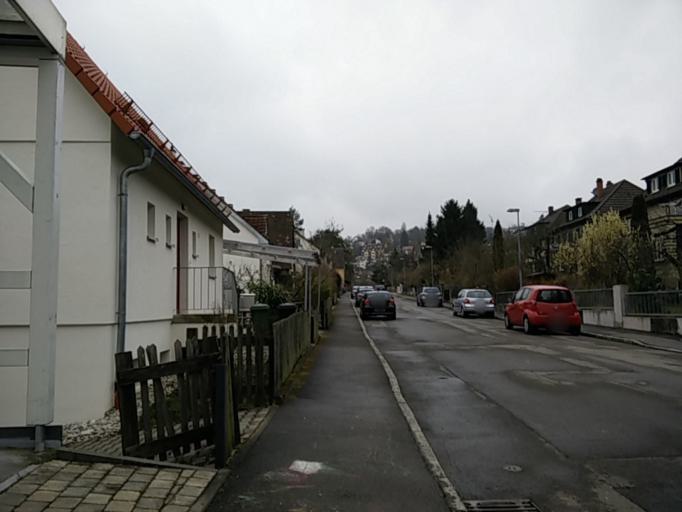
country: DE
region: Baden-Wuerttemberg
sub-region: Tuebingen Region
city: Tuebingen
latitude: 48.5311
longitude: 9.0715
